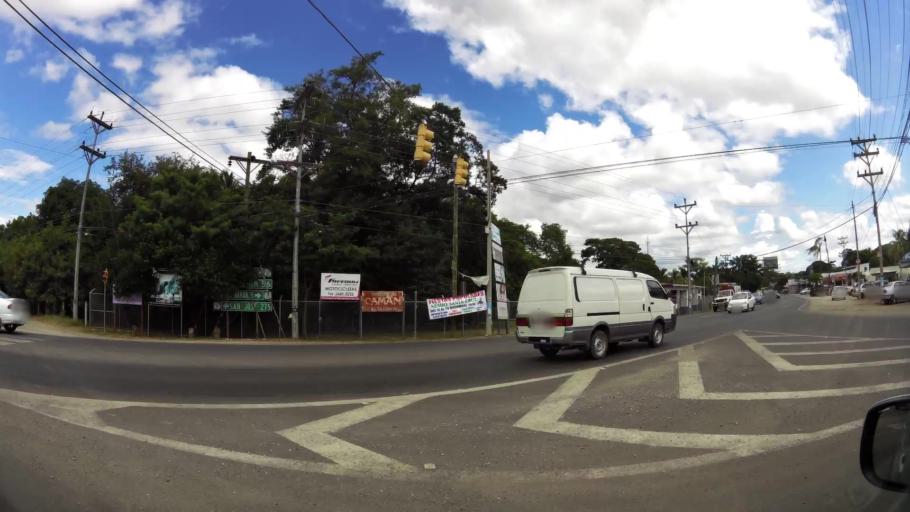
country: CR
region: Guanacaste
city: Santa Cruz
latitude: 10.2677
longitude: -85.5872
